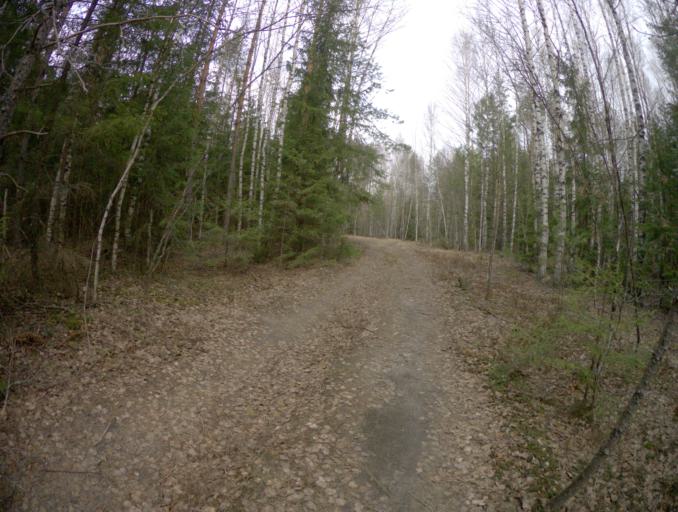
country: RU
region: Vladimir
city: Raduzhnyy
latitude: 55.9516
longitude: 40.2690
